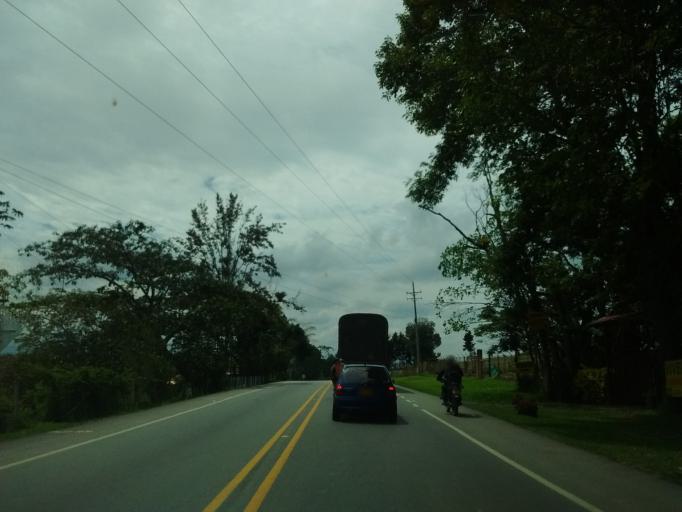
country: CO
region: Cauca
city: Cajibio
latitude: 2.5655
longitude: -76.5632
